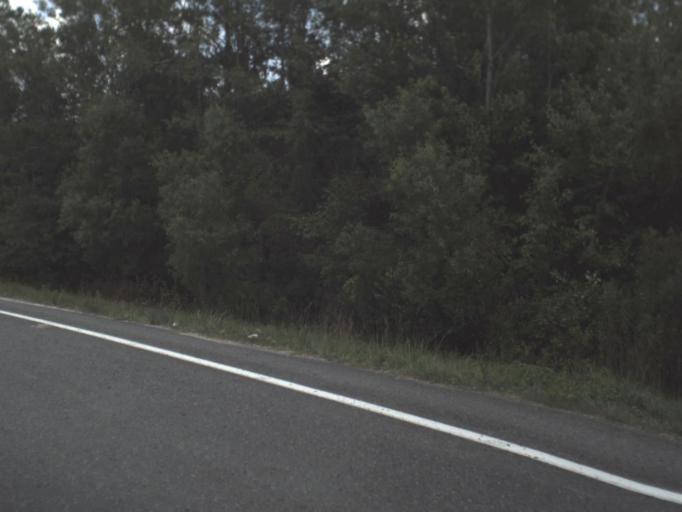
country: US
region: Florida
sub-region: Columbia County
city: Five Points
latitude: 30.2069
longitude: -82.6472
